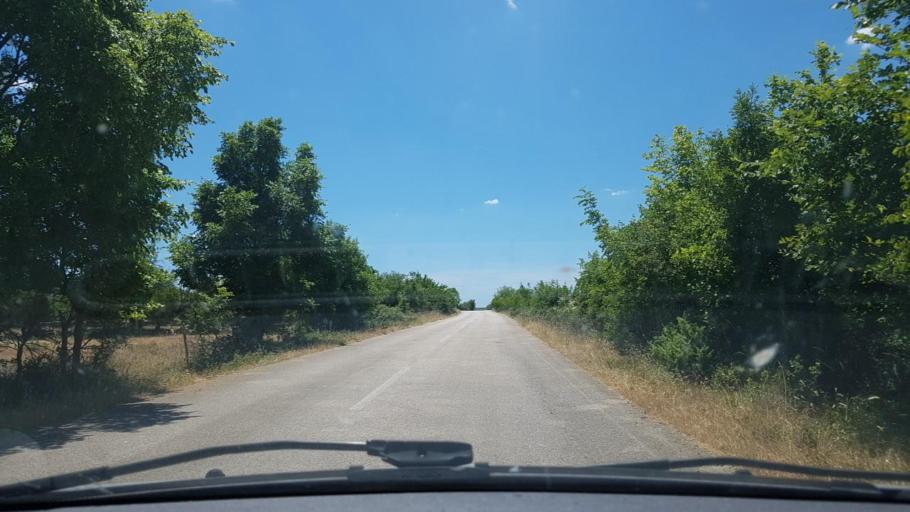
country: HR
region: Sibensko-Kniniska
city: Kistanje
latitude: 43.9754
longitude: 15.9701
